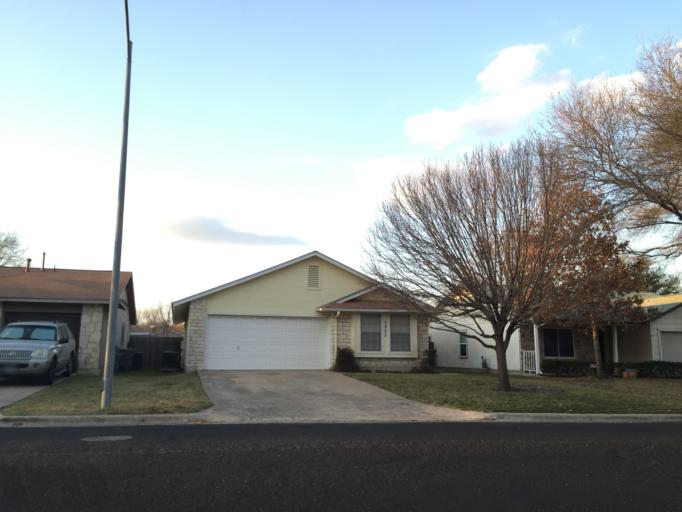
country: US
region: Texas
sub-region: Williamson County
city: Jollyville
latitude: 30.4382
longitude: -97.7416
